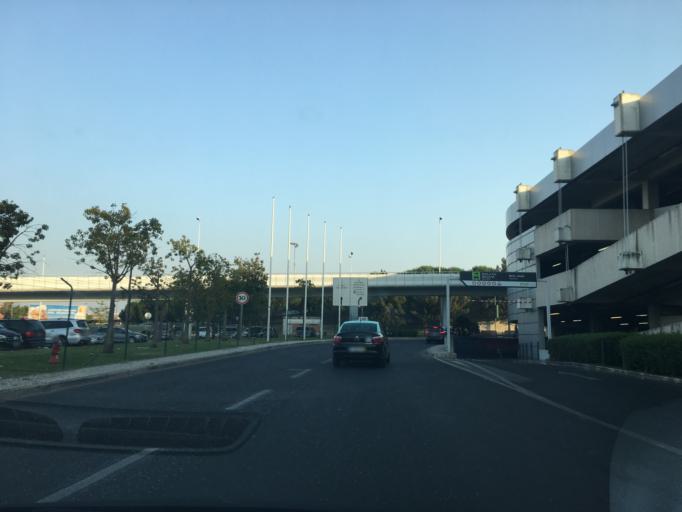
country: PT
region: Lisbon
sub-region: Loures
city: Moscavide
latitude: 38.7680
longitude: -9.1276
